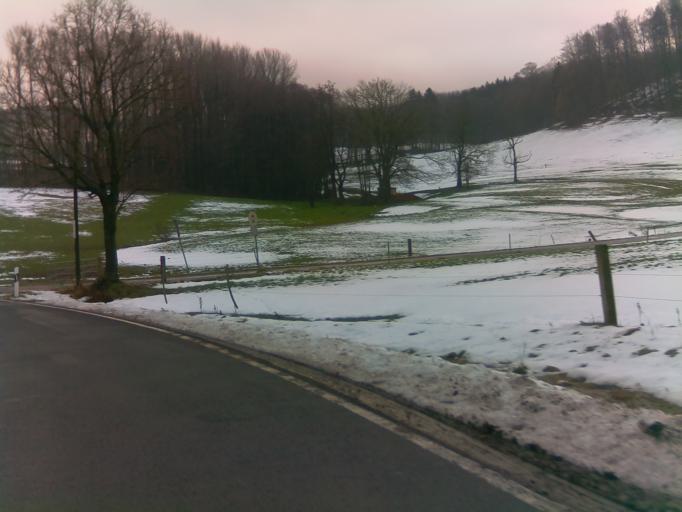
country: DE
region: Hesse
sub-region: Regierungsbezirk Kassel
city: Poppenhausen
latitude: 50.5269
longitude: 9.9287
